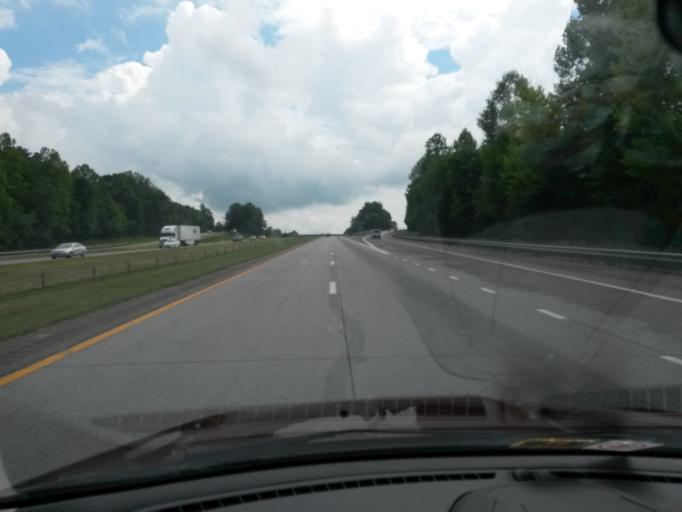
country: US
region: North Carolina
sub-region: Surry County
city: Elkin
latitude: 36.2854
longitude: -80.8190
